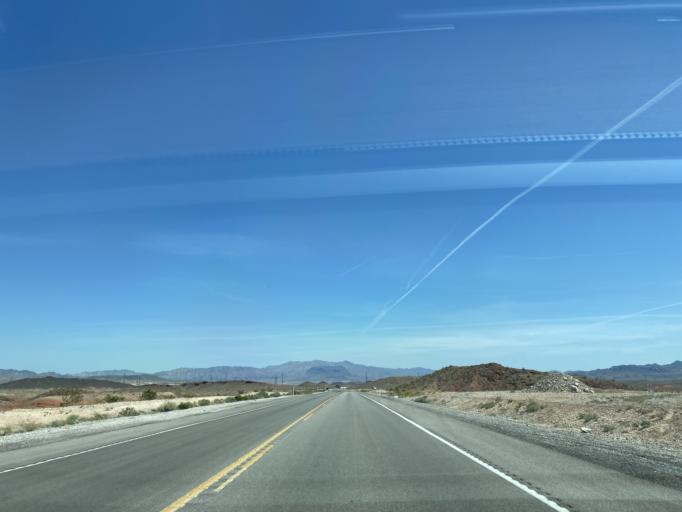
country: US
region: Nevada
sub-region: Clark County
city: Nellis Air Force Base
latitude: 36.1992
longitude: -114.9335
